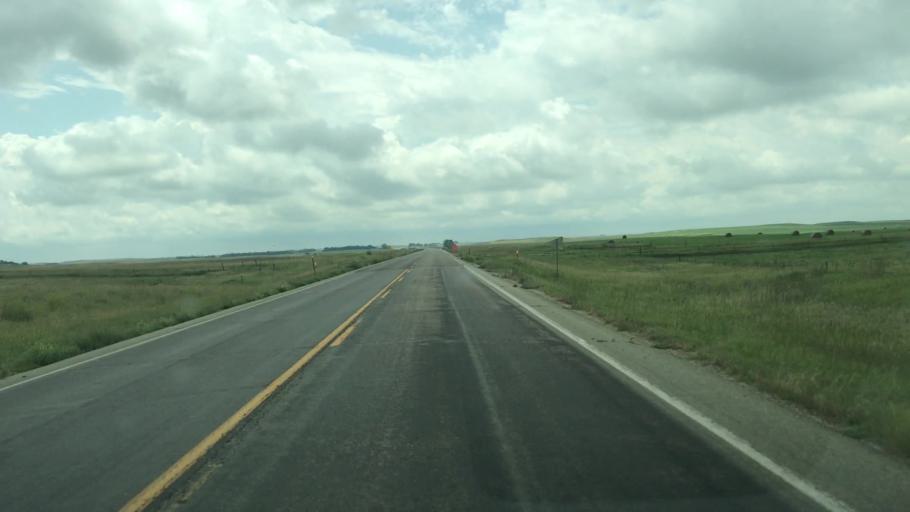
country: US
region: Nebraska
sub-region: Cherry County
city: Valentine
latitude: 43.0615
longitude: -100.5952
